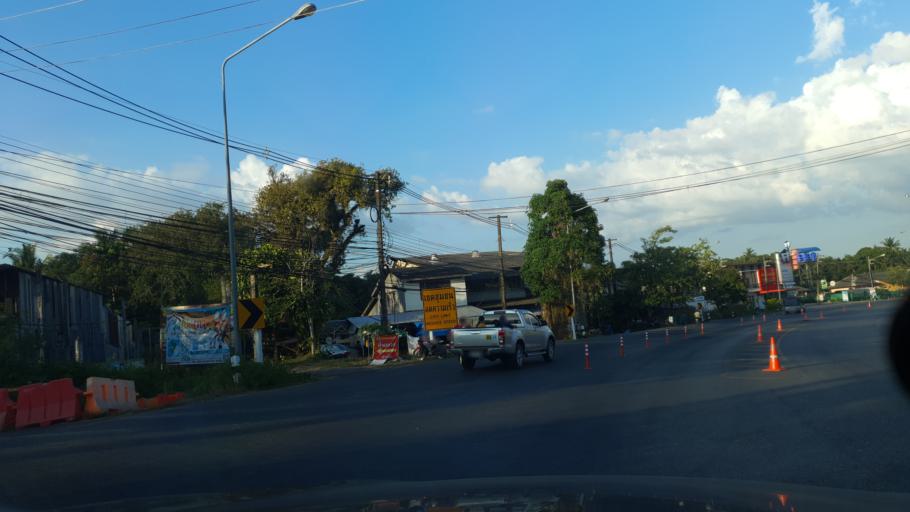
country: TH
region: Phangnga
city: Takua Pa
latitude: 8.8405
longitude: 98.2838
